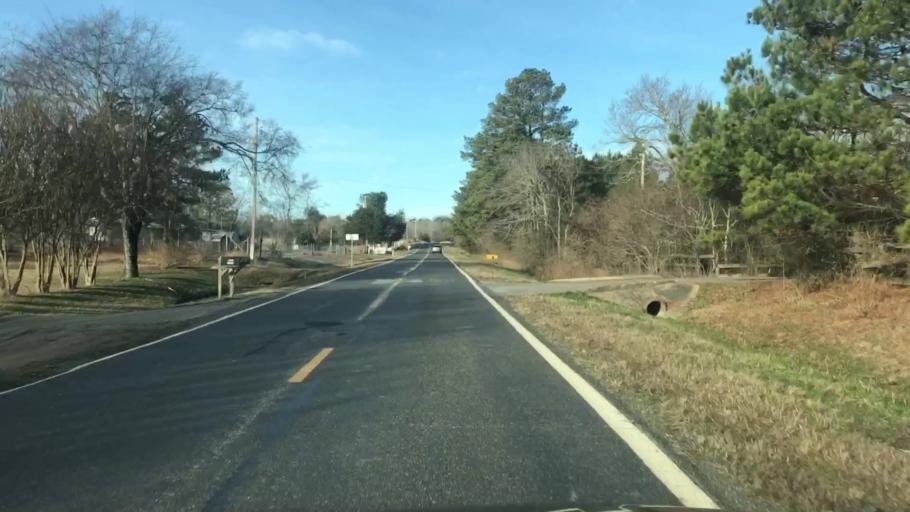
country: US
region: Arkansas
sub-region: Garland County
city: Rockwell
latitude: 34.4712
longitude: -93.2497
